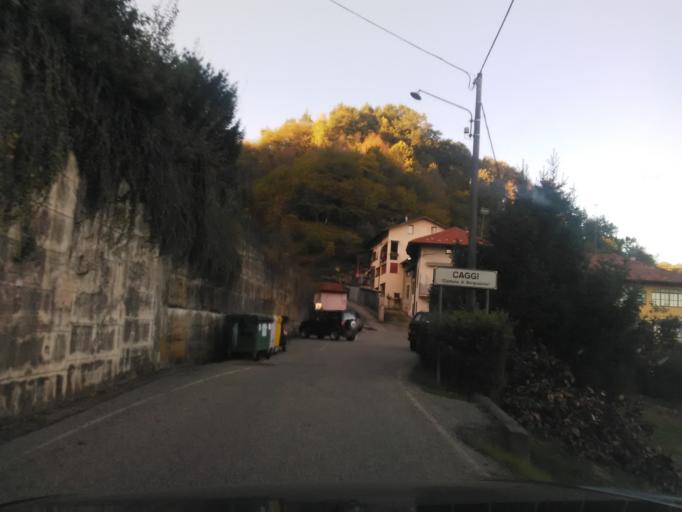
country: IT
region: Piedmont
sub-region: Provincia di Vercelli
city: Borgosesia
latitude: 45.7250
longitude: 8.2786
